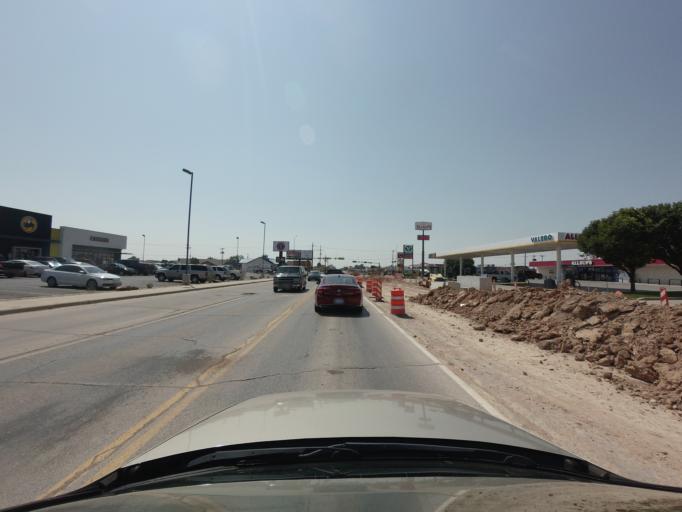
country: US
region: New Mexico
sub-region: Curry County
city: Clovis
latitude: 34.4348
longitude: -103.1964
